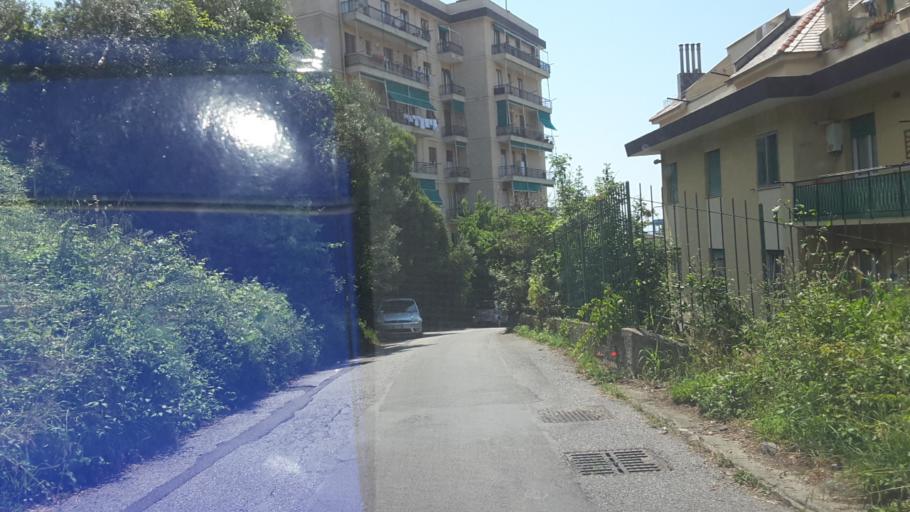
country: IT
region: Liguria
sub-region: Provincia di Genova
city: Mele
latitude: 44.4313
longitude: 8.7886
